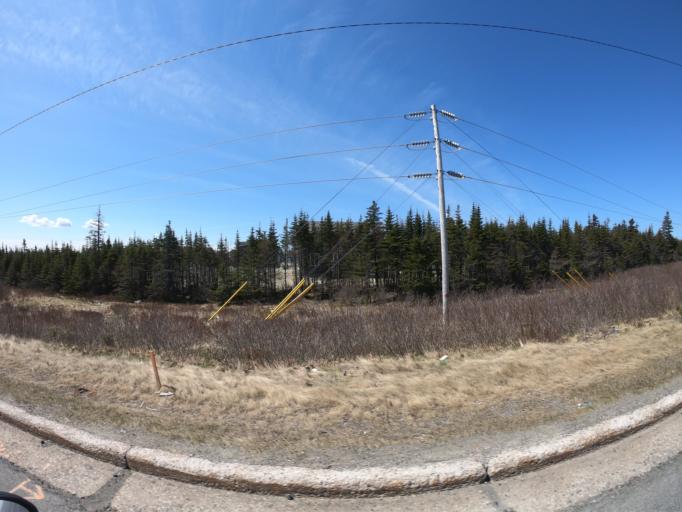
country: CA
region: Newfoundland and Labrador
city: Mount Pearl
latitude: 47.4992
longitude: -52.8127
